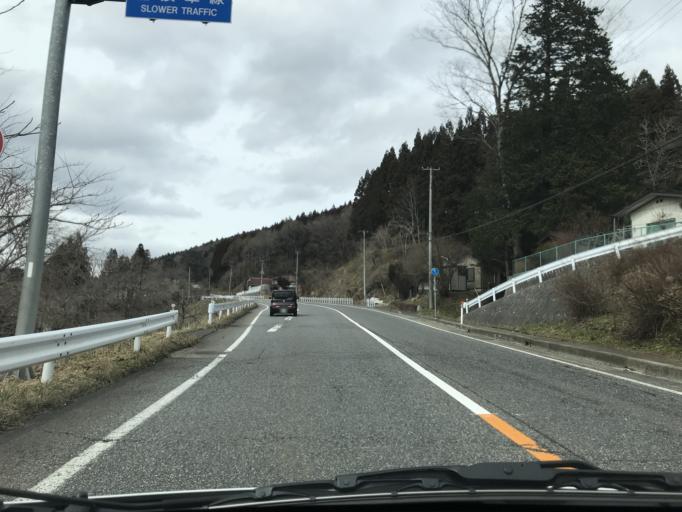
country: JP
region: Iwate
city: Tono
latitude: 39.3369
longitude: 141.4446
